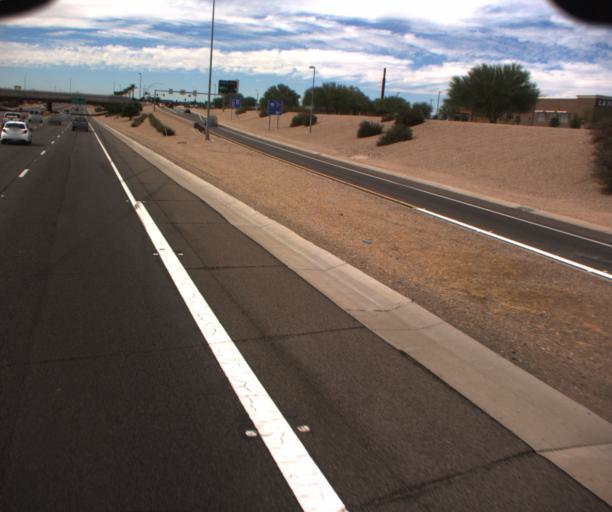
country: US
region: Arizona
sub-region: Maricopa County
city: Chandler
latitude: 33.2831
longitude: -111.7860
